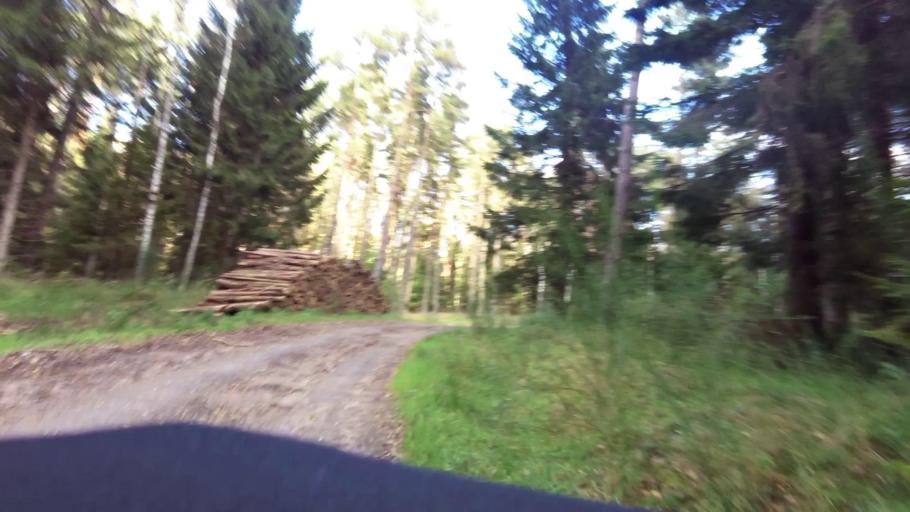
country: PL
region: West Pomeranian Voivodeship
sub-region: Powiat bialogardzki
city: Bialogard
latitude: 54.0434
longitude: 16.1349
